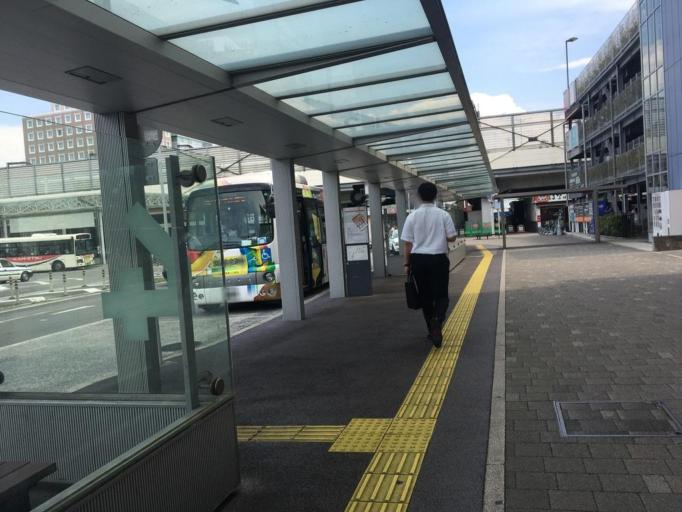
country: JP
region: Gunma
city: Maebashi-shi
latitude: 36.3838
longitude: 139.0721
